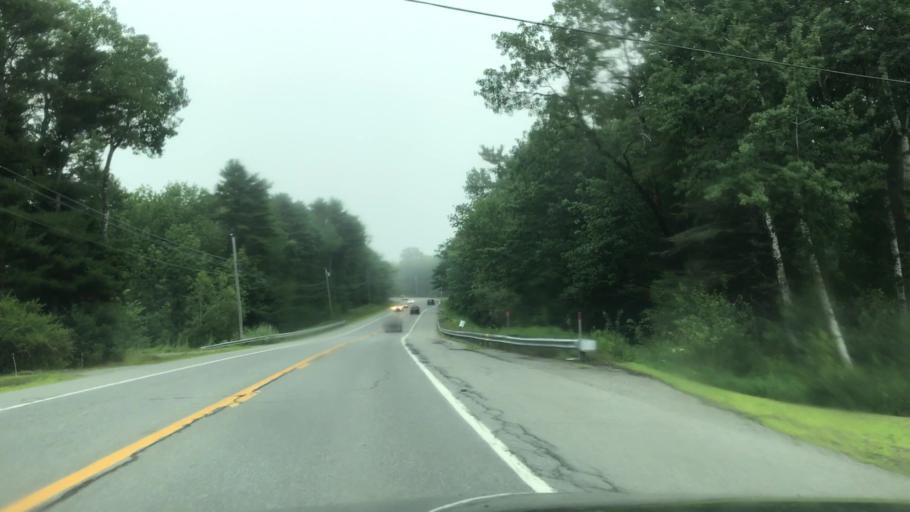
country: US
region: Maine
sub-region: Lincoln County
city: Waldoboro
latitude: 44.1024
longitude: -69.4264
